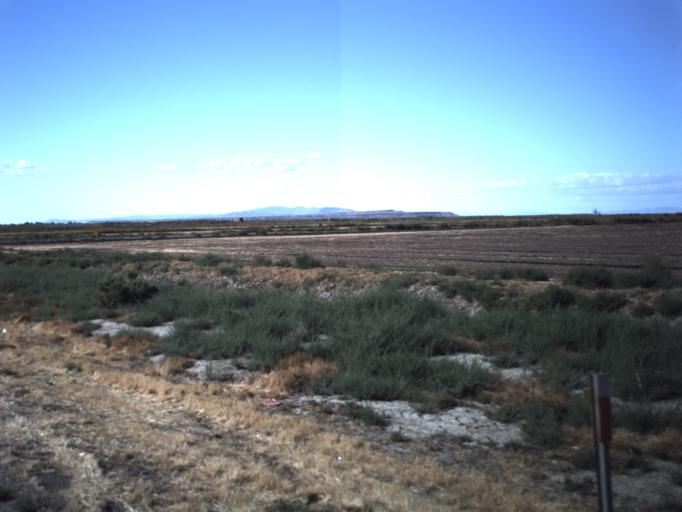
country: US
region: Utah
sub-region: Millard County
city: Delta
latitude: 39.3173
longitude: -112.6524
